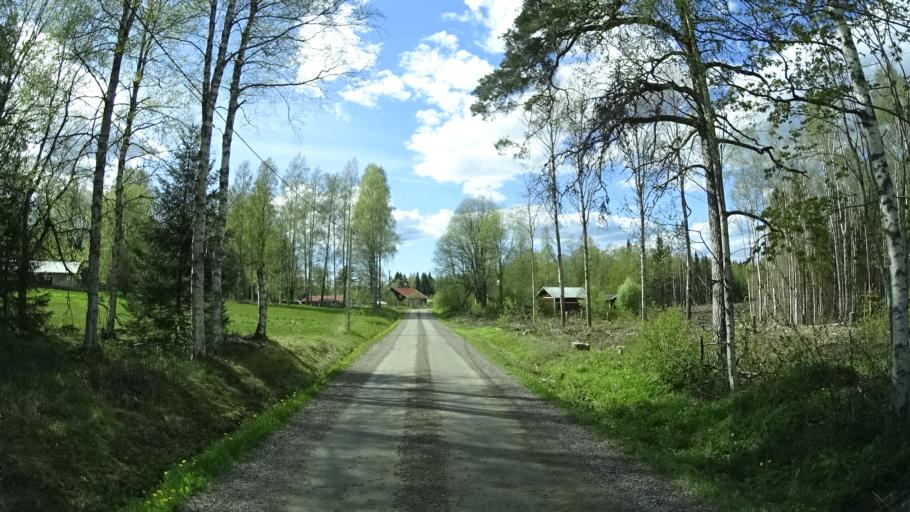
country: SE
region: OErebro
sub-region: Nora Kommun
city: As
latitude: 59.4365
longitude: 14.8594
